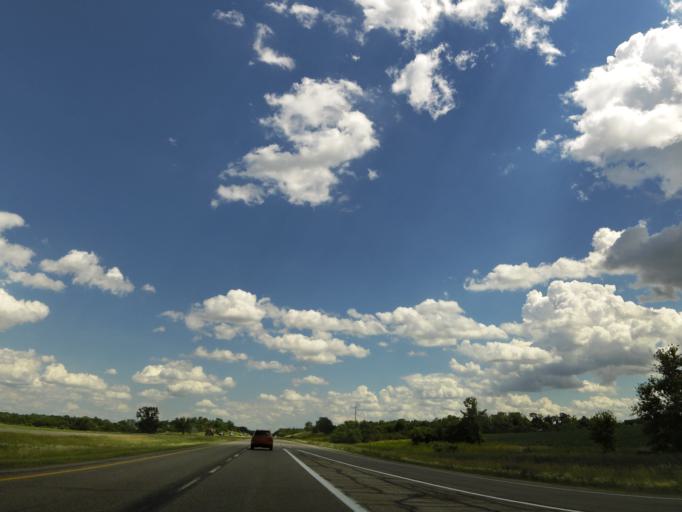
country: US
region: Iowa
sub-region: Benton County
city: Urbana
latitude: 42.2271
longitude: -91.8647
